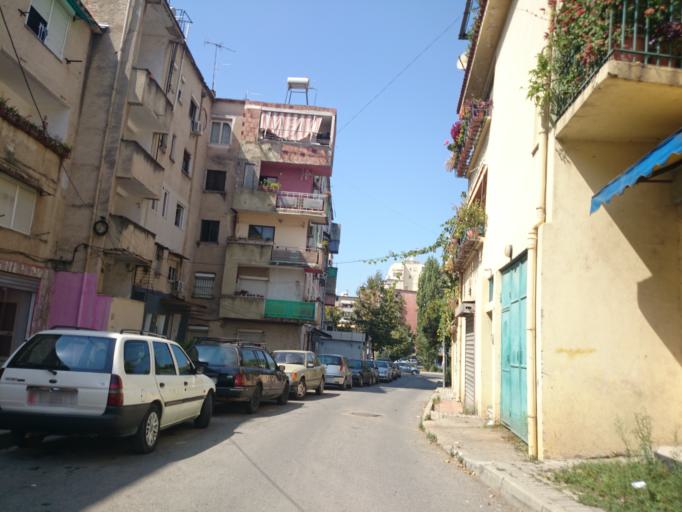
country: AL
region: Tirane
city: Tirana
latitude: 41.3293
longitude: 19.8339
